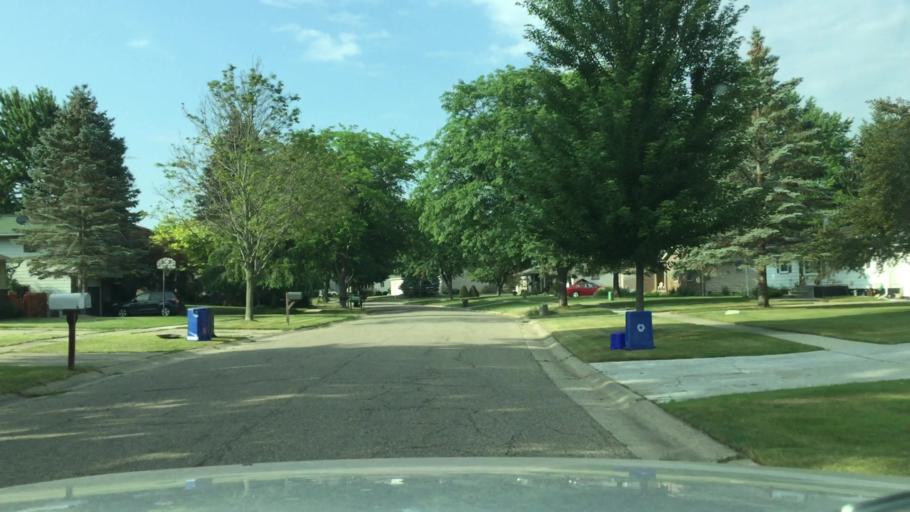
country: US
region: Michigan
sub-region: Genesee County
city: Flushing
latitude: 43.0585
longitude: -83.8651
